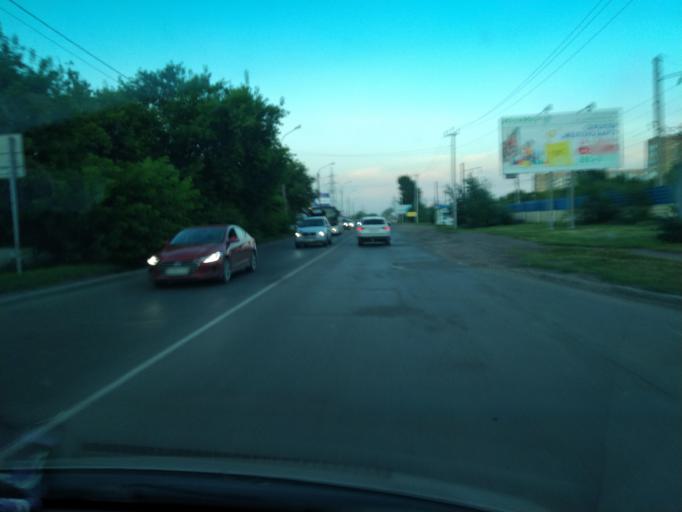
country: RU
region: Krasnoyarskiy
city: Krasnoyarsk
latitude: 55.9833
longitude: 92.8736
